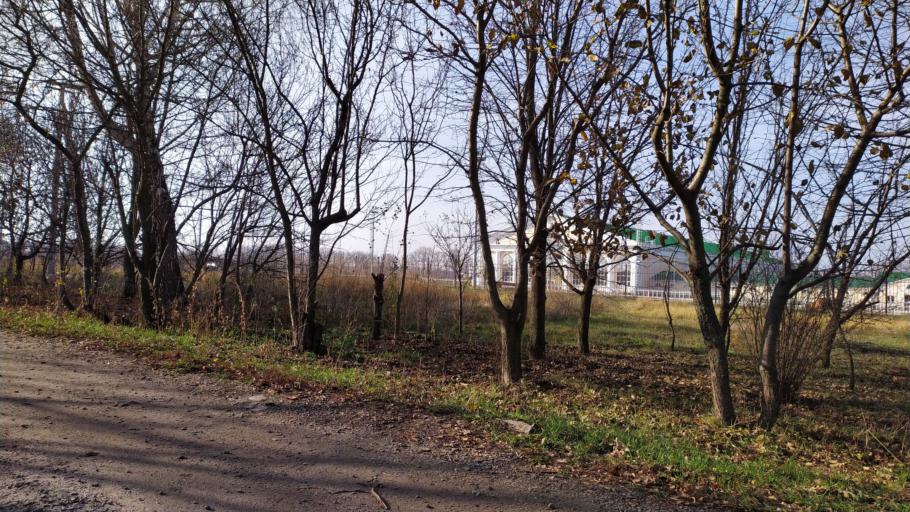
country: RU
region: Kursk
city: Kursk
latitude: 51.6420
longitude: 36.1313
